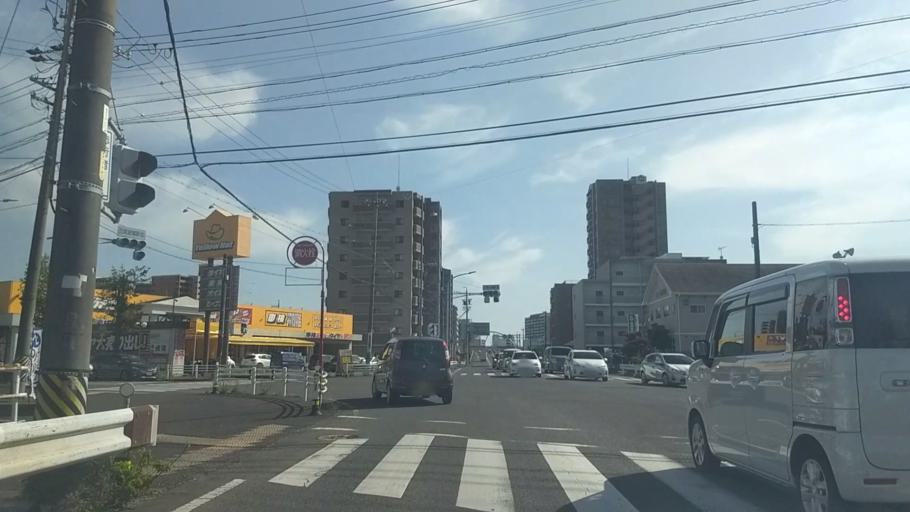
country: JP
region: Aichi
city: Anjo
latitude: 34.9739
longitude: 137.0632
